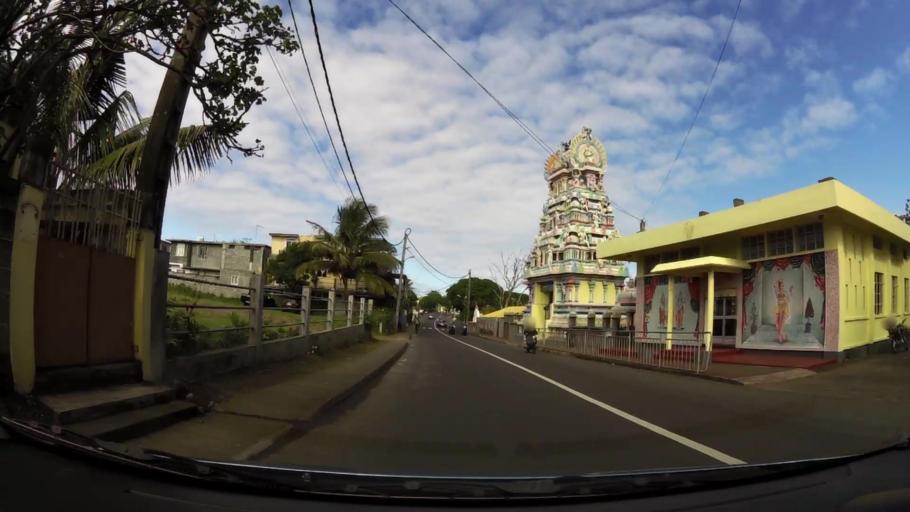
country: MU
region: Grand Port
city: Beau Vallon
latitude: -20.4180
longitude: 57.7042
